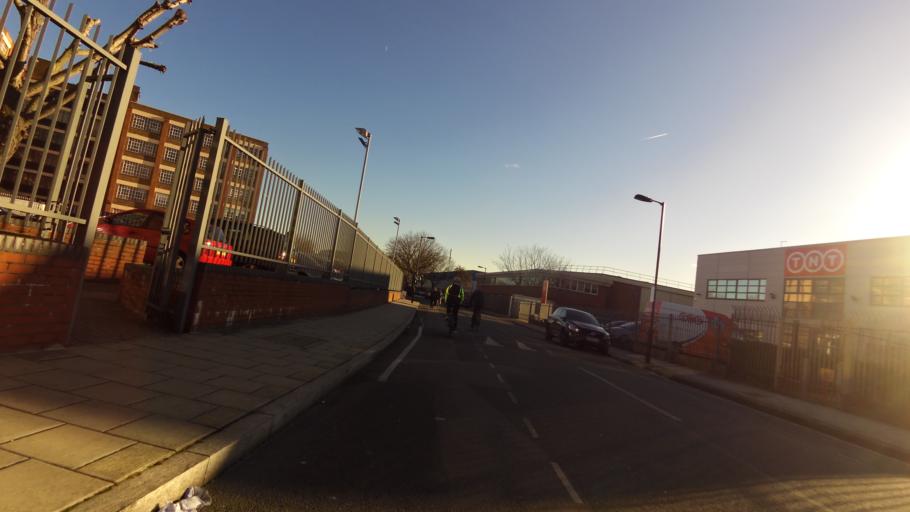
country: GB
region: England
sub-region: Greater London
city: City of London
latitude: 51.4940
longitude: -0.0796
